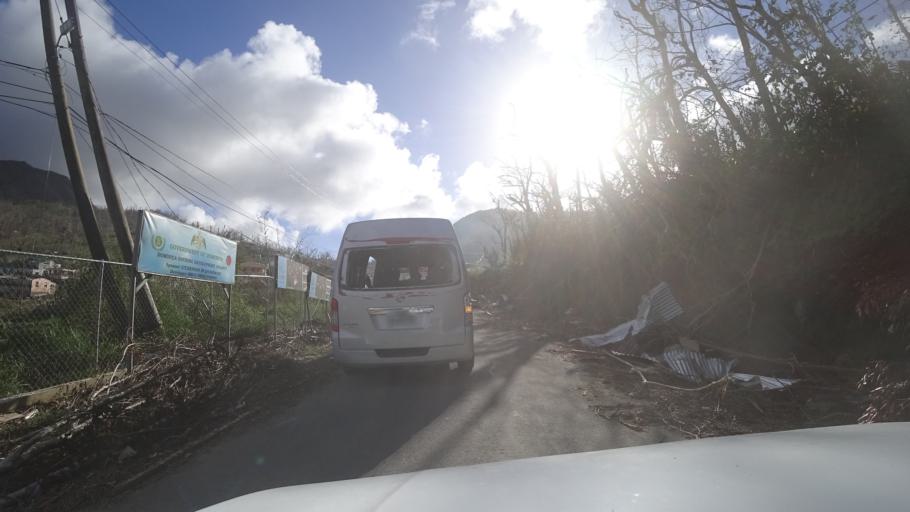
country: DM
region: Saint Luke
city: Pointe Michel
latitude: 15.2675
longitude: -61.3465
